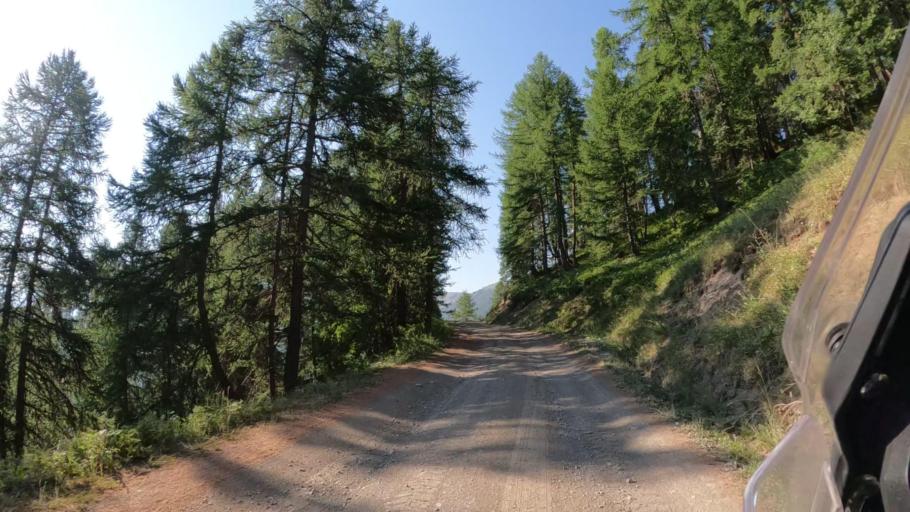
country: FR
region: Provence-Alpes-Cote d'Azur
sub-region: Departement des Hautes-Alpes
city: Guillestre
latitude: 44.6209
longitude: 6.6237
